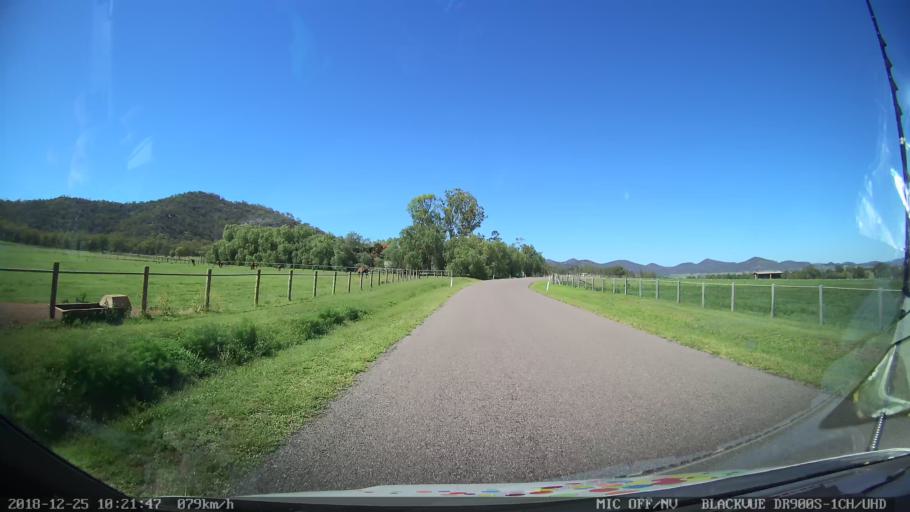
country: AU
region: New South Wales
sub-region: Muswellbrook
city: Denman
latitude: -32.3713
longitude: 150.5394
